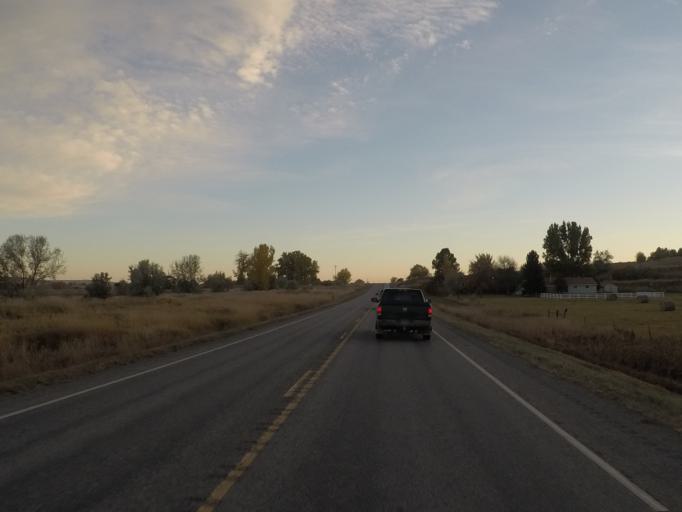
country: US
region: Montana
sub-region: Yellowstone County
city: Laurel
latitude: 45.5517
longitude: -108.8434
